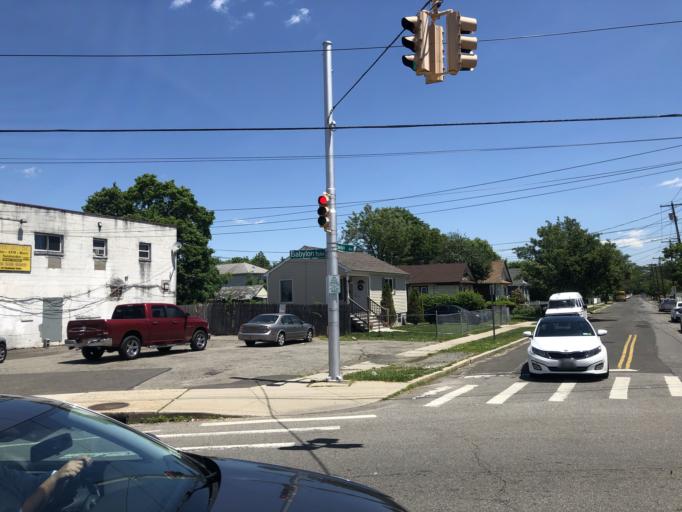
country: US
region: New York
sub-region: Nassau County
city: Roosevelt
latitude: 40.6746
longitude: -73.5829
